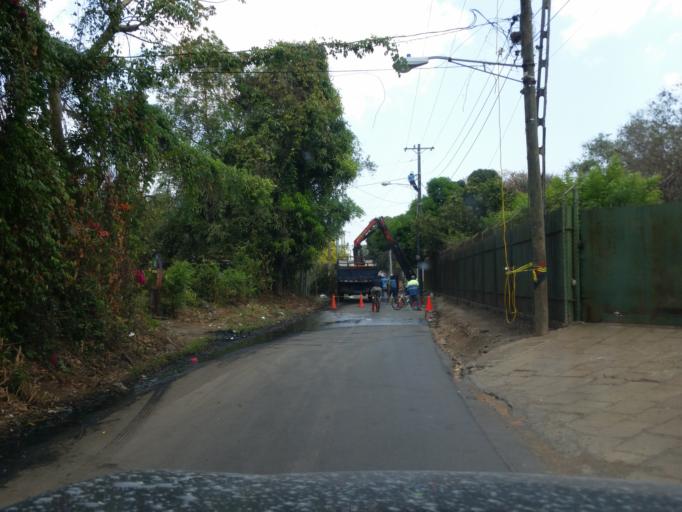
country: NI
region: Masaya
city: Ticuantepe
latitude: 12.0653
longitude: -86.2075
